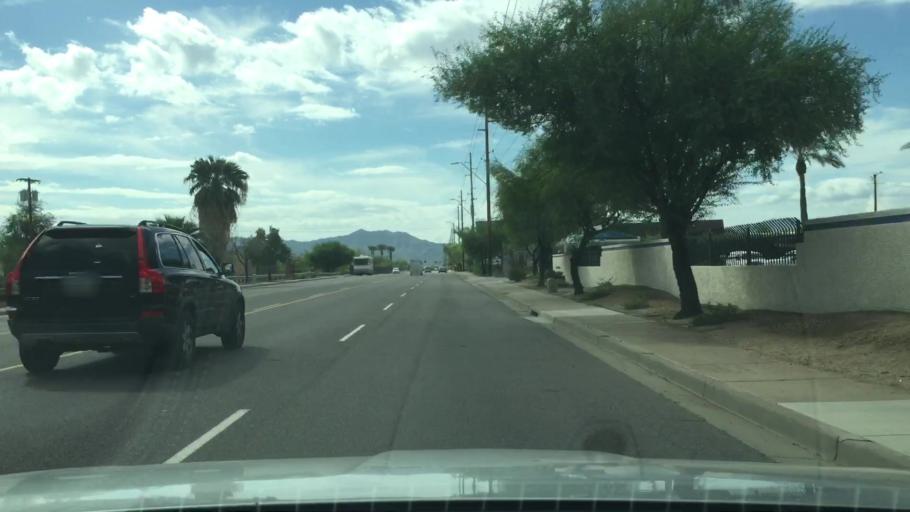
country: US
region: Arizona
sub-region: Maricopa County
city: Phoenix
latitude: 33.4281
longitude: -112.1346
